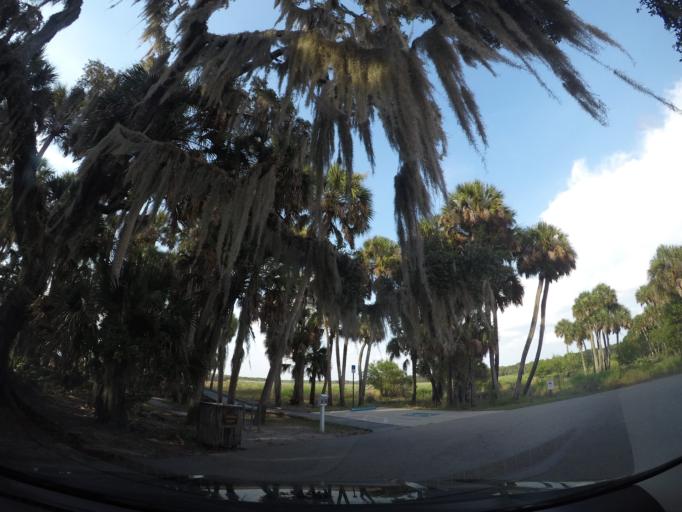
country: US
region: Florida
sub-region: Sarasota County
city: Lake Sarasota
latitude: 27.2749
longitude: -82.2703
